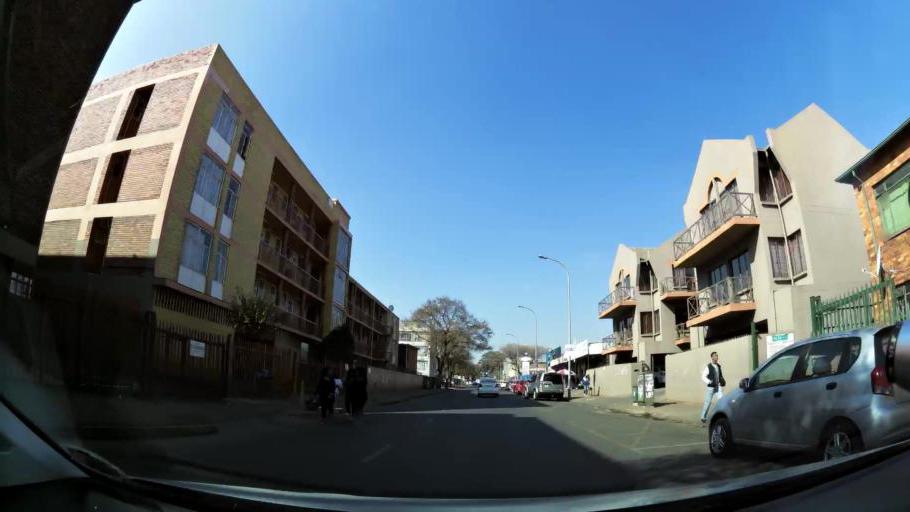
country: ZA
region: Gauteng
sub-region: City of Johannesburg Metropolitan Municipality
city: Modderfontein
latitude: -26.1051
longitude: 28.2333
